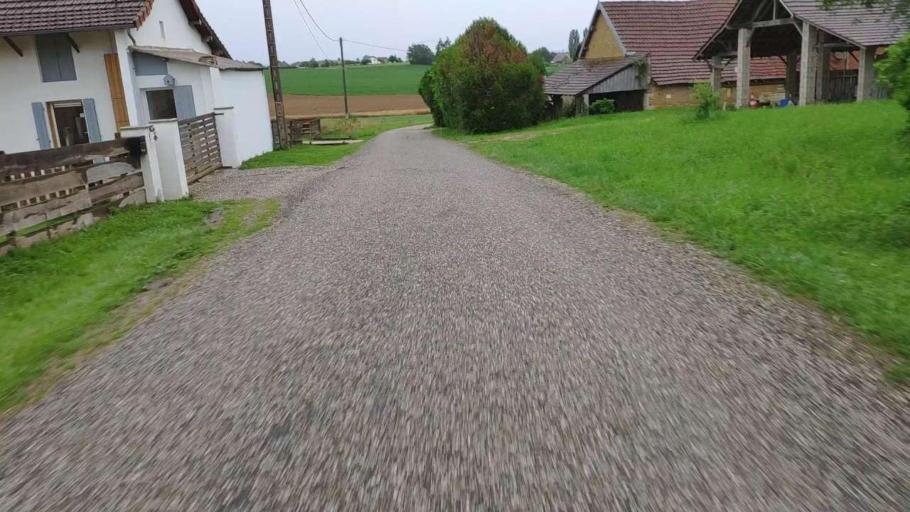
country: FR
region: Franche-Comte
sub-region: Departement du Jura
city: Chaussin
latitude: 46.8751
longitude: 5.4153
